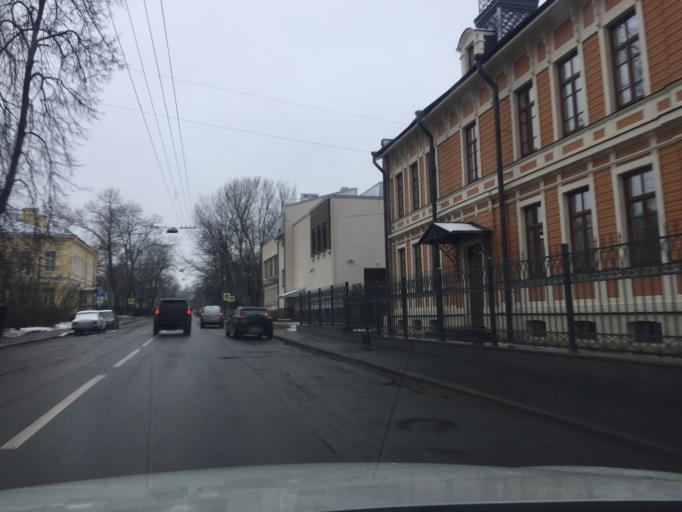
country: RU
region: St.-Petersburg
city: Pushkin
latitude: 59.7184
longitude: 30.4040
